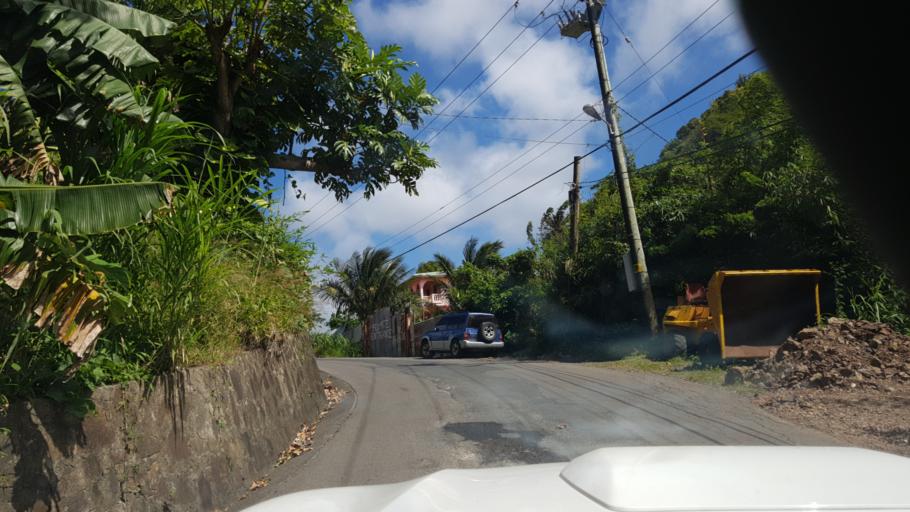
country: LC
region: Castries Quarter
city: Bisee
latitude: 13.9941
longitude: -60.9738
